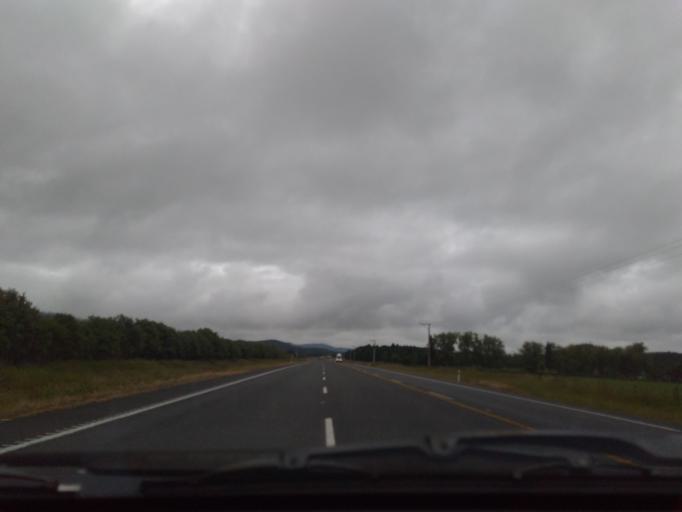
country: NZ
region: Northland
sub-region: Whangarei
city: Ruakaka
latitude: -36.0159
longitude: 174.4184
